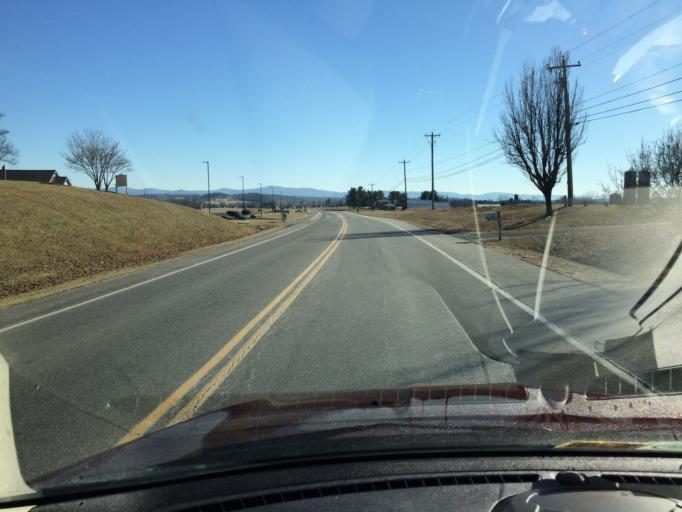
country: US
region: Virginia
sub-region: Rockingham County
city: Bridgewater
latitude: 38.3708
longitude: -78.9504
